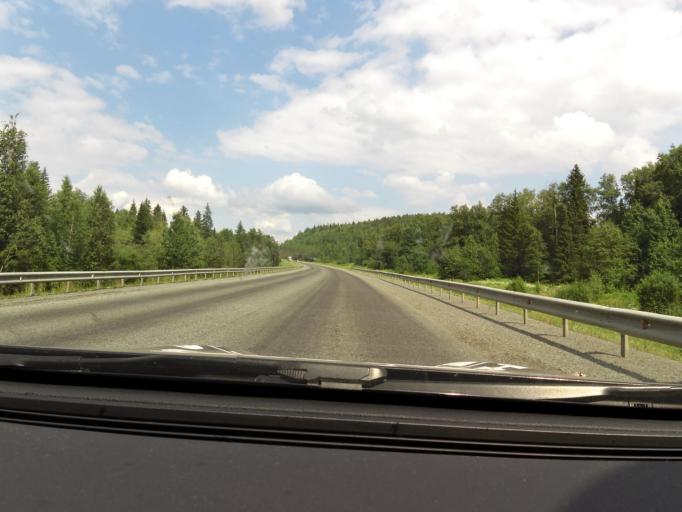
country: RU
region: Sverdlovsk
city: Arti
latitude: 56.7824
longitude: 58.4215
